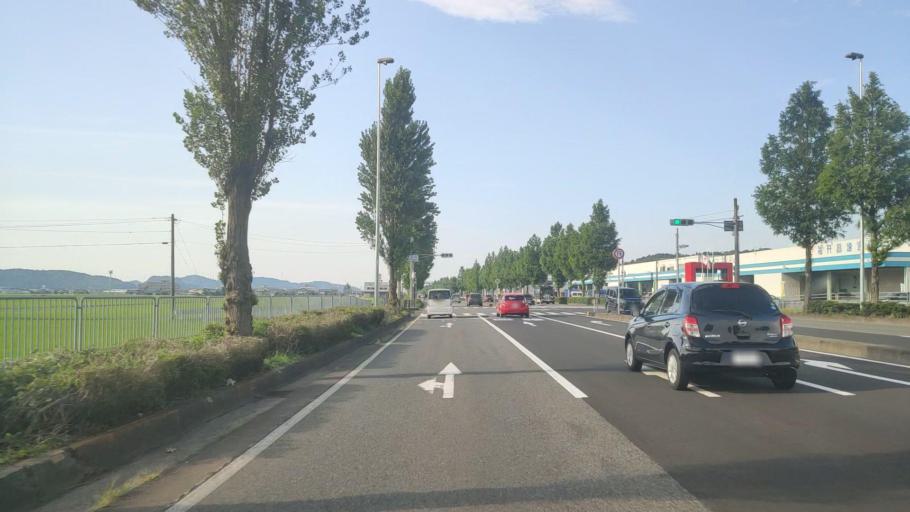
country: JP
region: Fukui
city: Sabae
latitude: 35.9959
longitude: 136.2059
